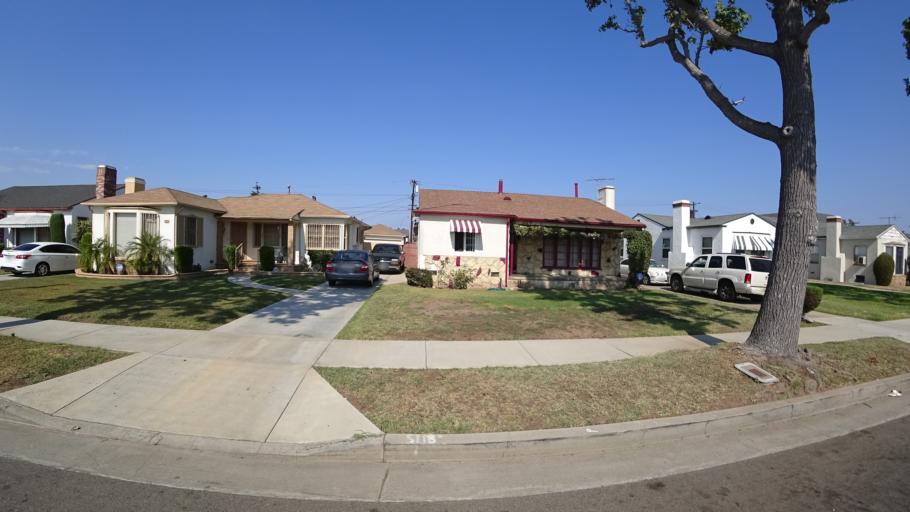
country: US
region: California
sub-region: Los Angeles County
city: Westmont
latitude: 33.9535
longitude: -118.3134
